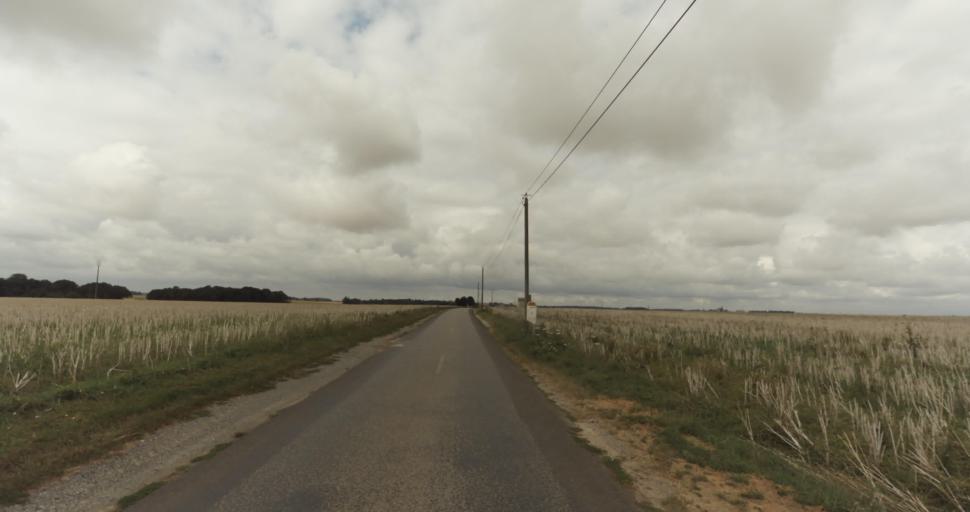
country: FR
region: Haute-Normandie
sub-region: Departement de l'Eure
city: La Couture-Boussey
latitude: 48.9323
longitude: 1.3555
